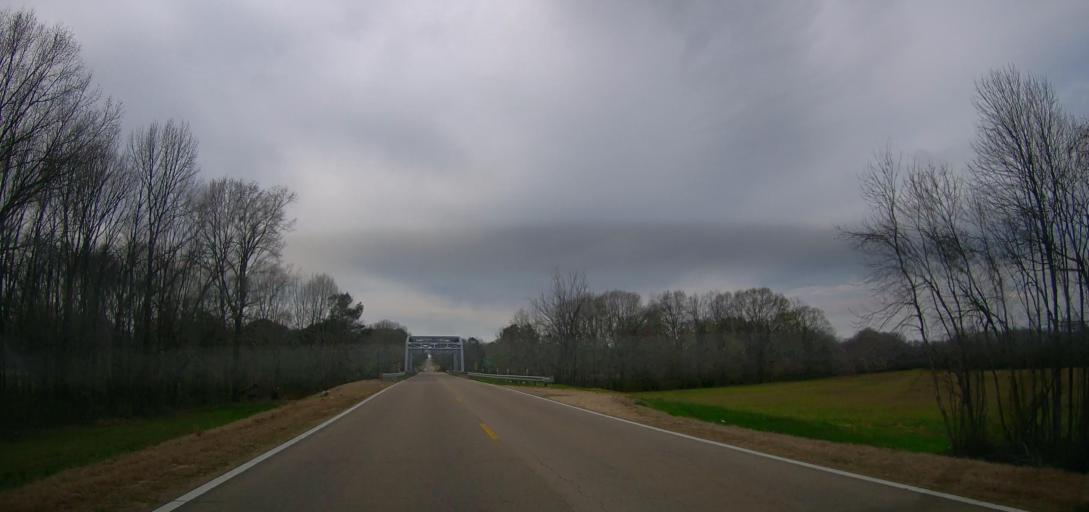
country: US
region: Mississippi
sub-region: Itawamba County
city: Fulton
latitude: 34.2523
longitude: -88.4751
